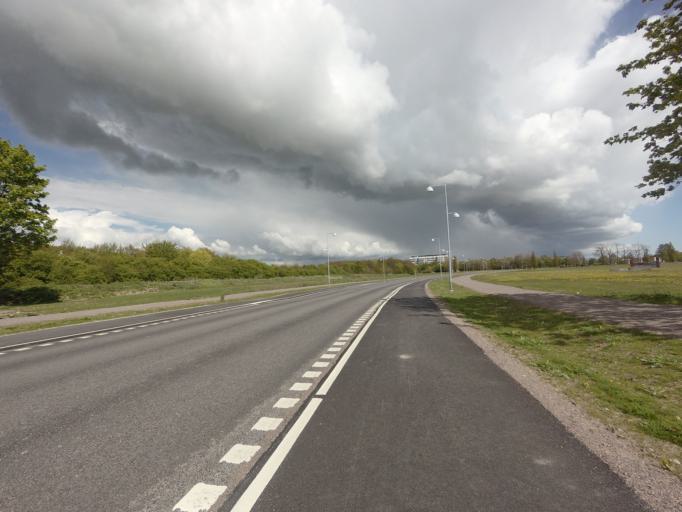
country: SE
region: Skane
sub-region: Landskrona
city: Landskrona
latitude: 55.8947
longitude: 12.8405
